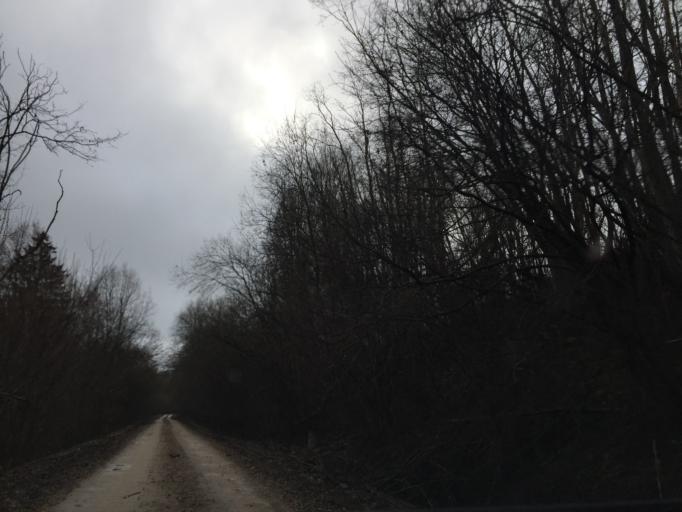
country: LV
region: Broceni
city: Broceni
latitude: 56.6820
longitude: 22.5578
